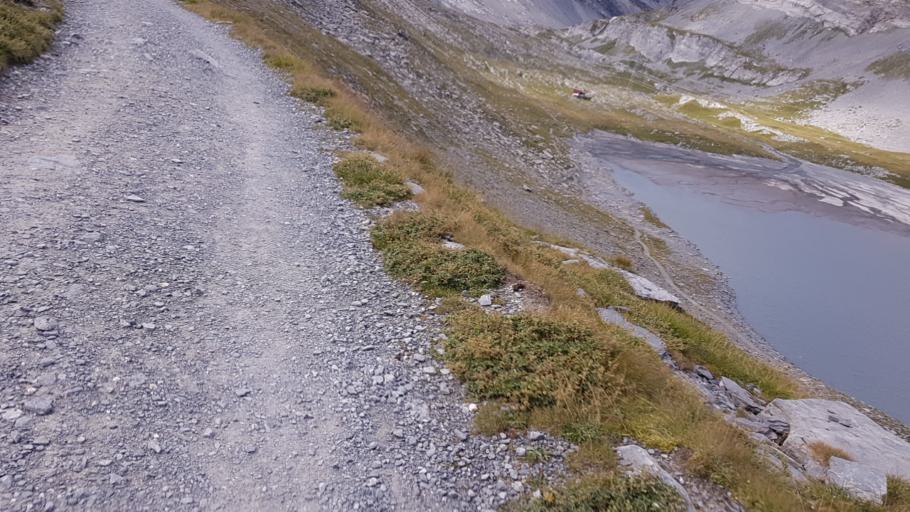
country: CH
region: Valais
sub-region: Leuk District
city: Leukerbad
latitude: 46.4073
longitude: 7.6218
